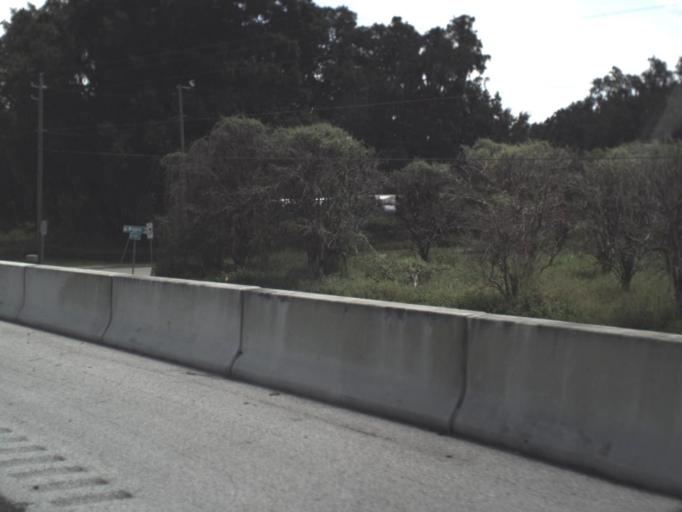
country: US
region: Florida
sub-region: Hillsborough County
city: Plant City
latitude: 28.0367
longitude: -82.0688
